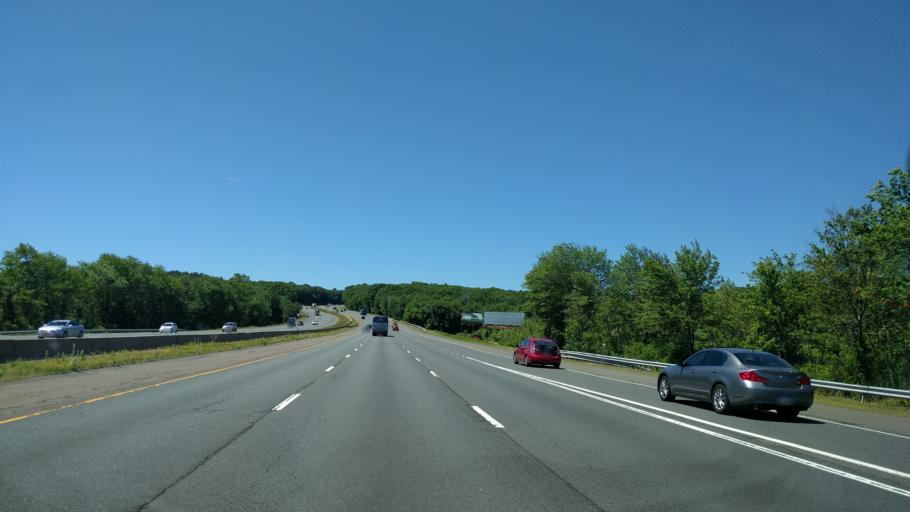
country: US
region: Connecticut
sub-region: Tolland County
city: Tolland
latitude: 41.8623
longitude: -72.3648
